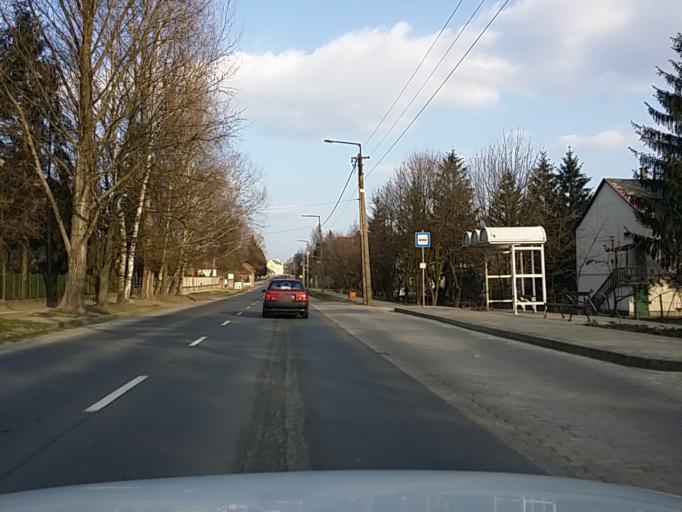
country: HU
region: Borsod-Abauj-Zemplen
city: Putnok
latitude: 48.2963
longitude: 20.4233
